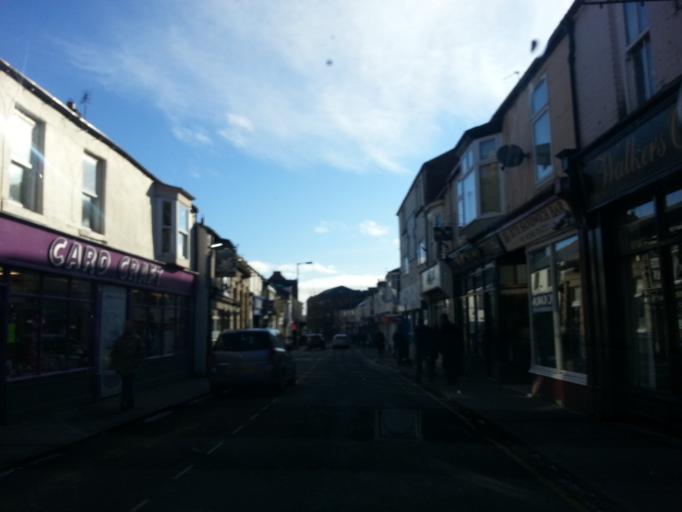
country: GB
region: England
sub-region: County Durham
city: Crook
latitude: 54.7161
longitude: -1.7471
